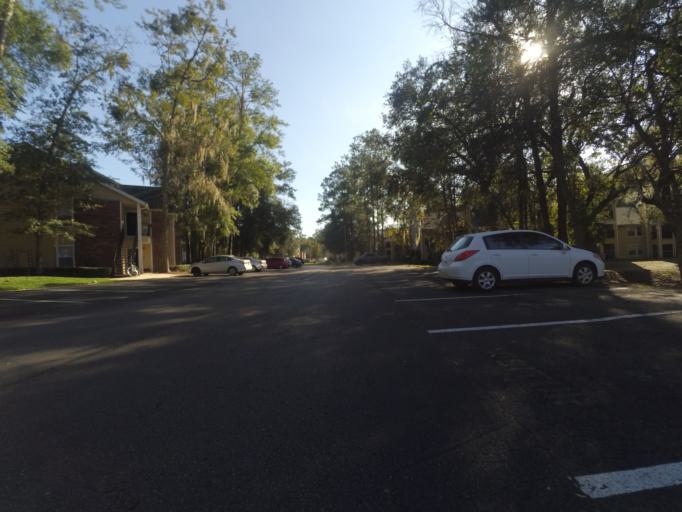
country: US
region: Florida
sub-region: Alachua County
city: Gainesville
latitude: 29.6166
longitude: -82.3578
